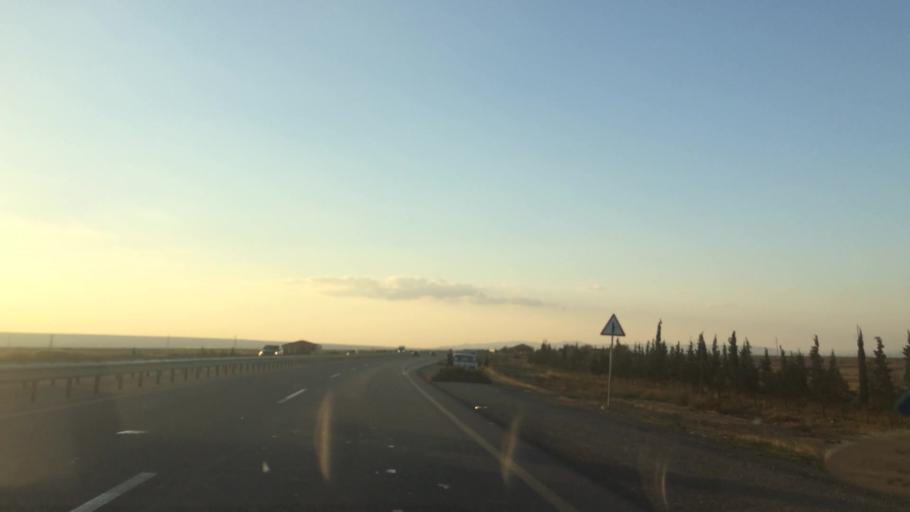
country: AZ
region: Baki
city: Qobustan
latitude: 39.9834
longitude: 49.2154
